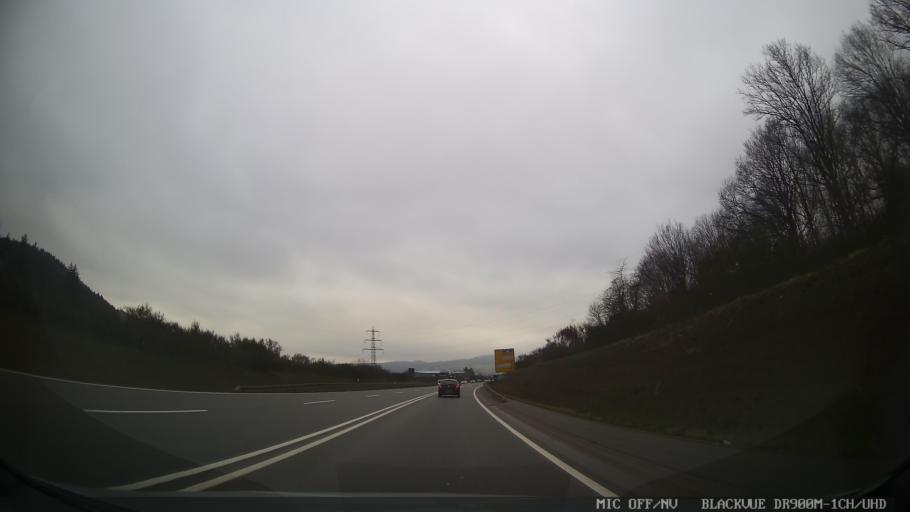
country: DE
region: Saarland
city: Merzig
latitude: 49.4702
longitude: 6.6296
